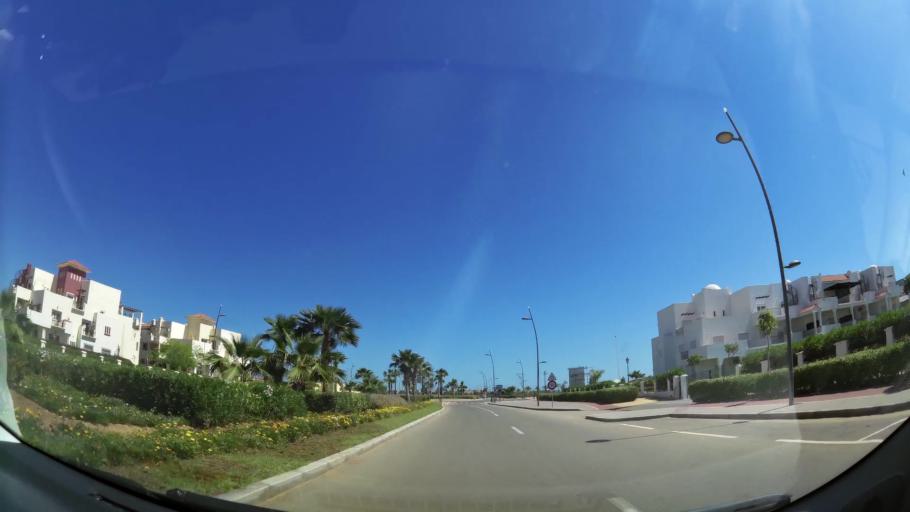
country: MA
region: Oriental
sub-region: Berkane-Taourirt
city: Madagh
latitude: 35.0987
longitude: -2.3001
